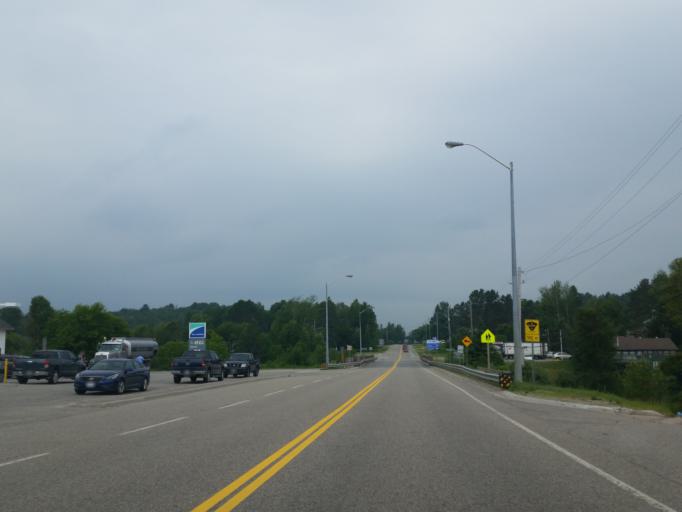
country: CA
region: Ontario
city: Bancroft
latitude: 45.4934
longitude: -78.2382
